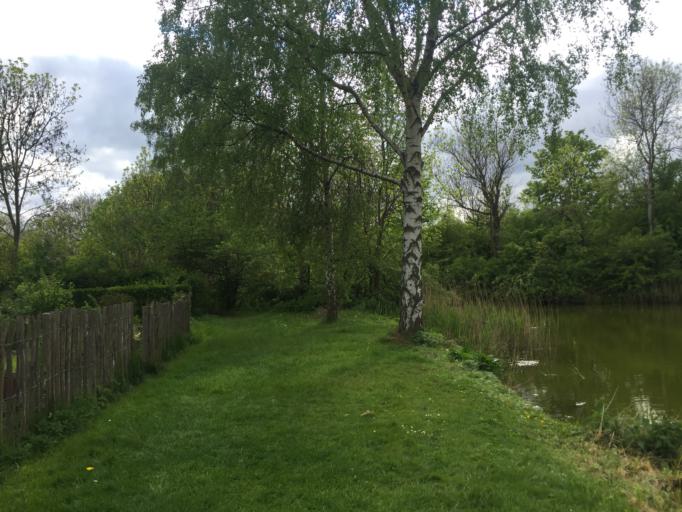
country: DK
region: Capital Region
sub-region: Kobenhavn
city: Christianshavn
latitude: 55.6792
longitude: 12.6136
